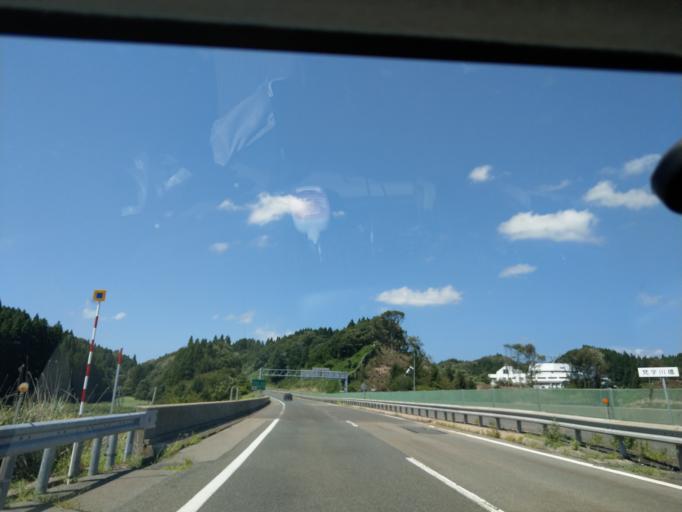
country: JP
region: Akita
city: Akita
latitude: 39.6517
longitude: 140.2051
